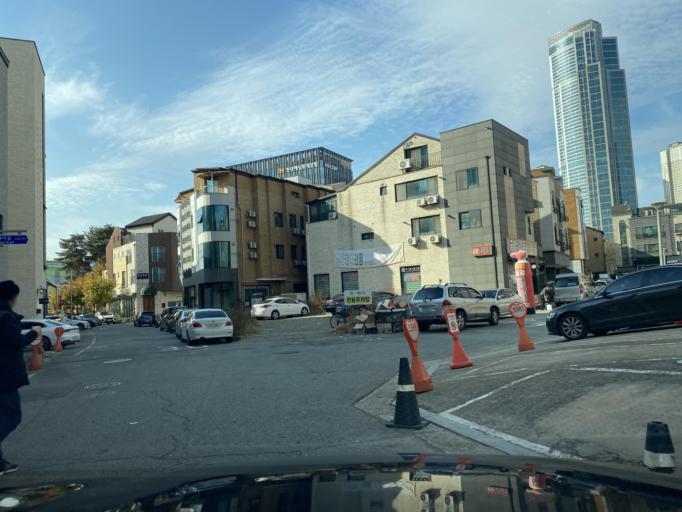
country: KR
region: Chungcheongnam-do
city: Cheonan
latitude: 36.8000
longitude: 127.1074
